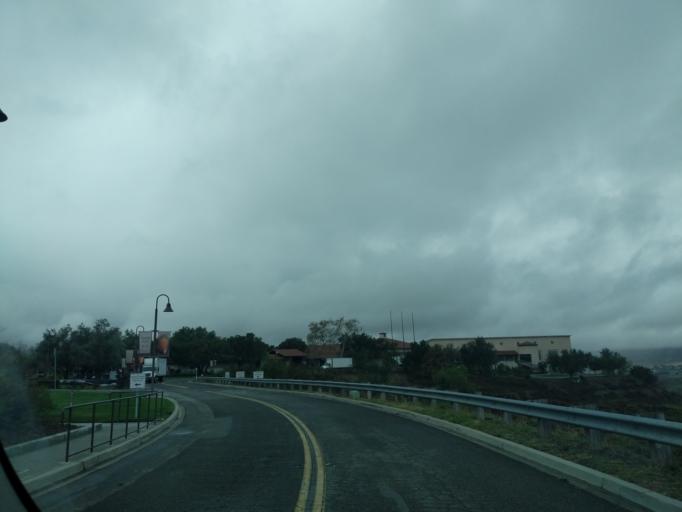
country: US
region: California
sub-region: Ventura County
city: Simi Valley
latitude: 34.2586
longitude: -118.8177
